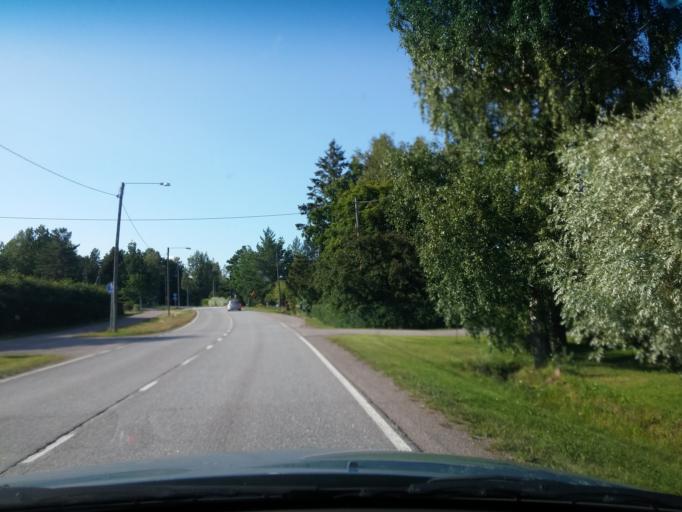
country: FI
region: Uusimaa
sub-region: Porvoo
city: Askola
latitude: 60.4977
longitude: 25.5364
